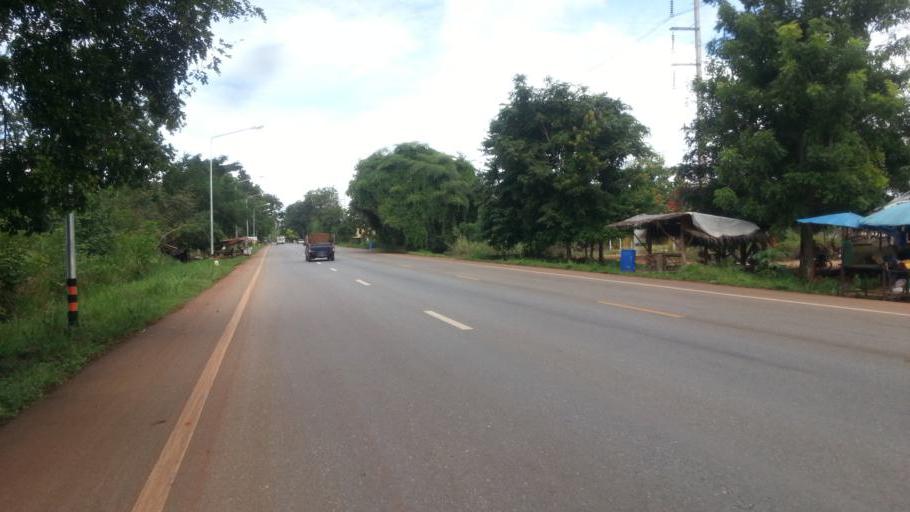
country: TH
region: Kanchanaburi
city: Sai Yok
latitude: 14.1153
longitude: 99.1892
